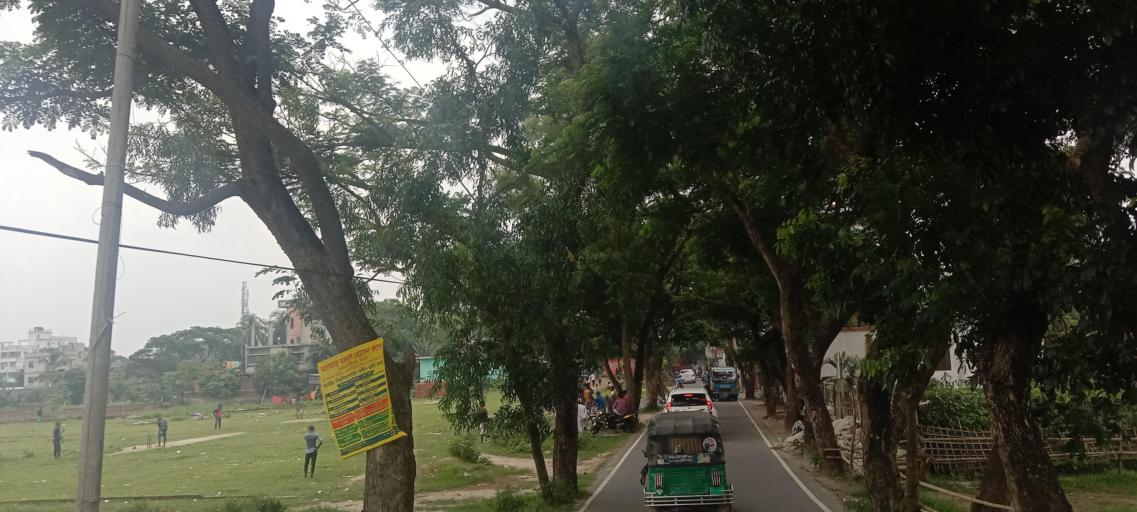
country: BD
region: Dhaka
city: Azimpur
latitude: 23.7124
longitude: 90.3454
